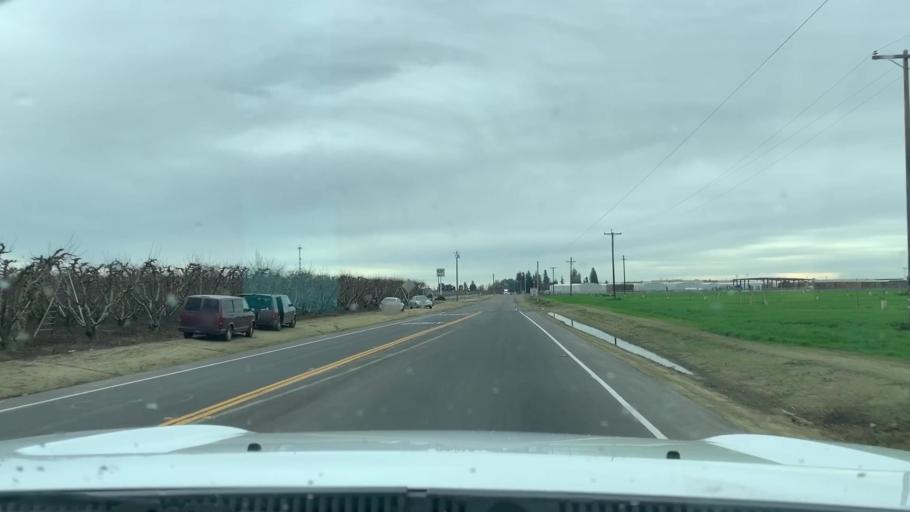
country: US
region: California
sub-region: Fresno County
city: Kingsburg
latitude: 36.5456
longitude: -119.5752
